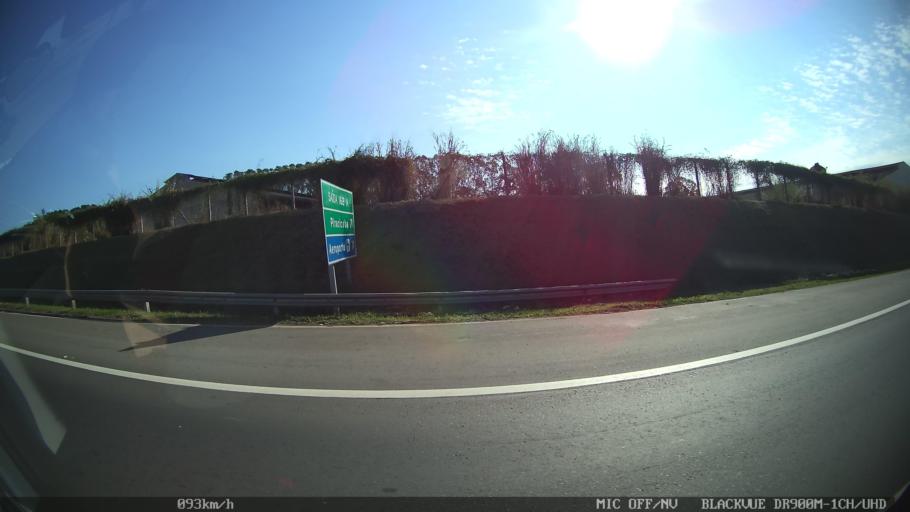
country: BR
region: Sao Paulo
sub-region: Piracicaba
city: Piracicaba
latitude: -22.7177
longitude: -47.6063
